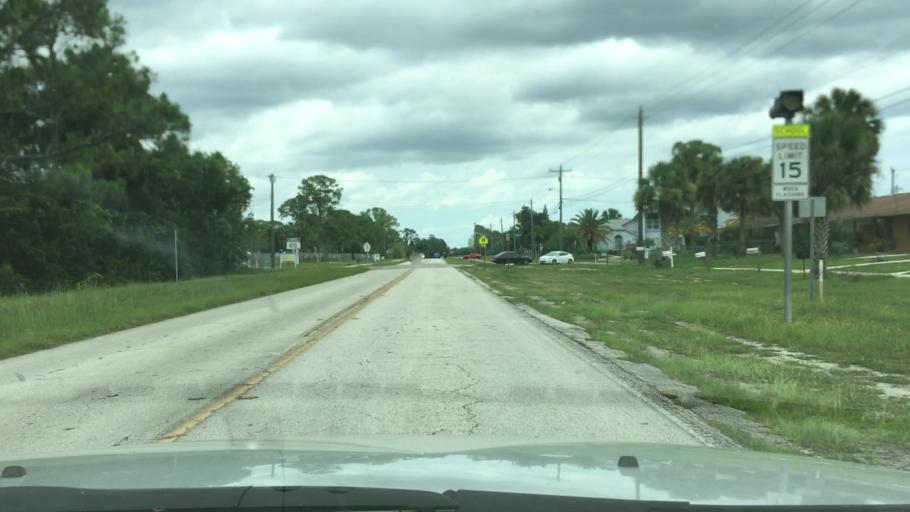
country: US
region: Florida
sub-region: Volusia County
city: Holly Hill
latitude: 29.2223
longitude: -81.0704
